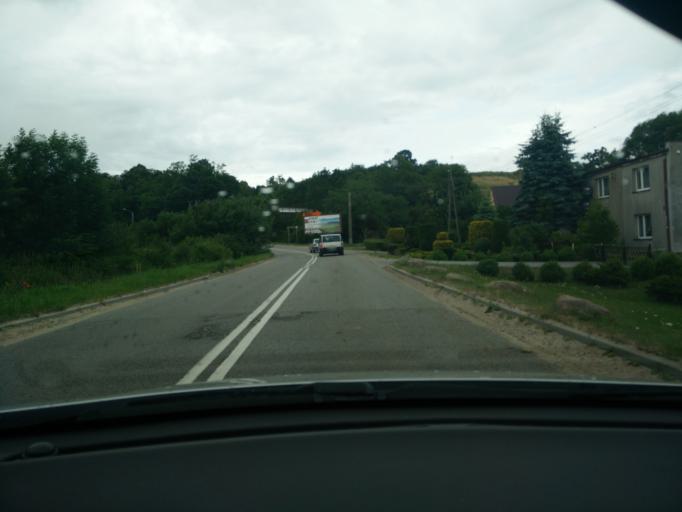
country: PL
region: Pomeranian Voivodeship
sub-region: Powiat pucki
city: Mrzezino
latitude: 54.6477
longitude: 18.4351
